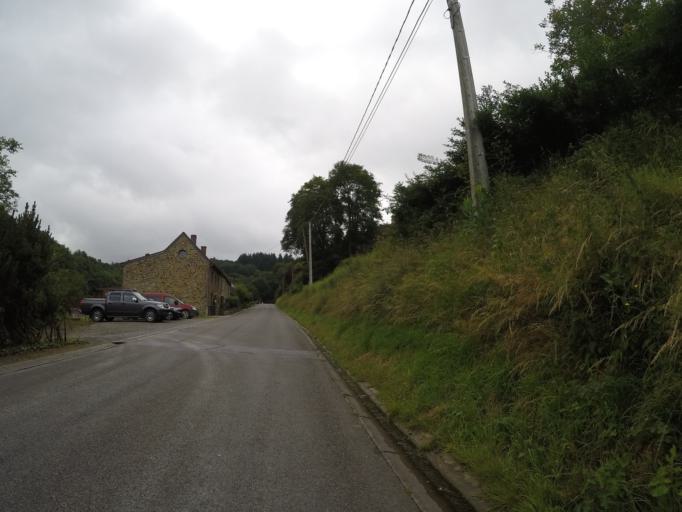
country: BE
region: Wallonia
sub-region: Province de Namur
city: Assesse
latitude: 50.3440
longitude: 4.9569
